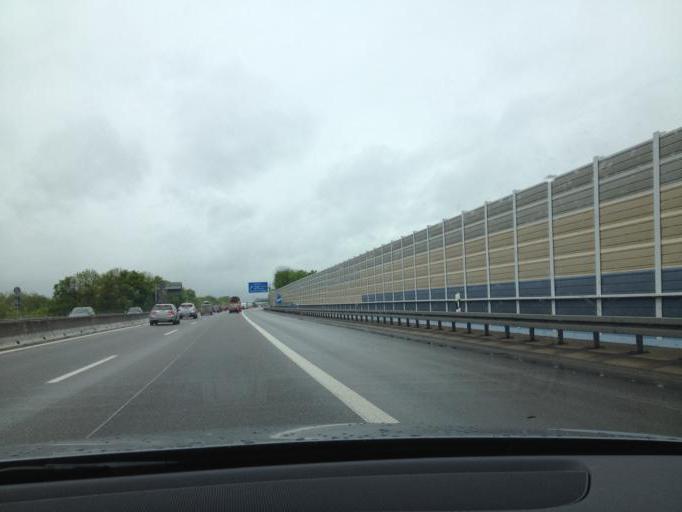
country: DE
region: Baden-Wuerttemberg
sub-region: Regierungsbezirk Stuttgart
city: Neckarsulm
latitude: 49.1855
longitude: 9.2037
